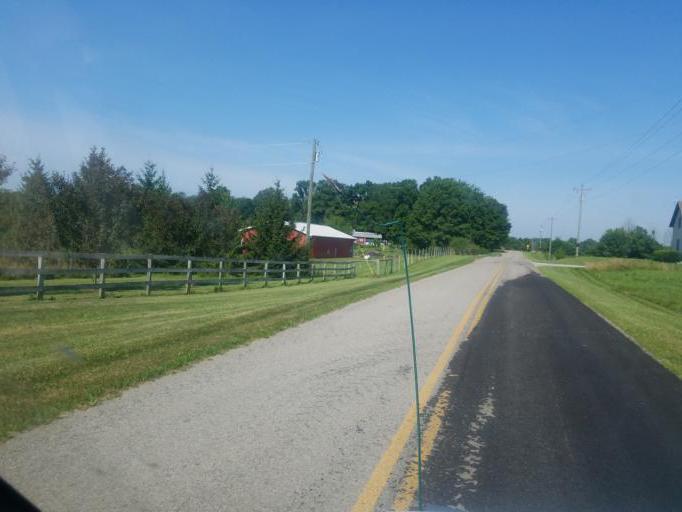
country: US
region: Ohio
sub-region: Union County
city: Marysville
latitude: 40.2843
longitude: -83.2848
